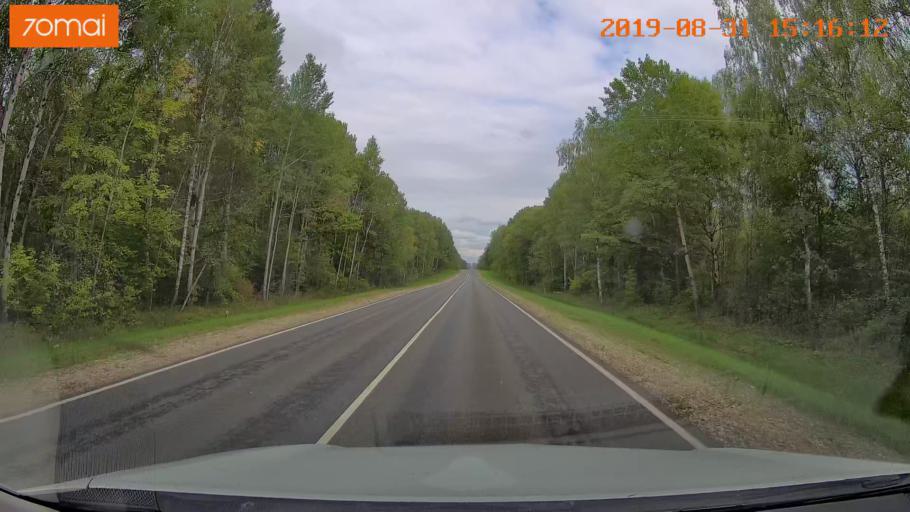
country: RU
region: Kaluga
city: Baryatino
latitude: 54.4579
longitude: 34.3446
